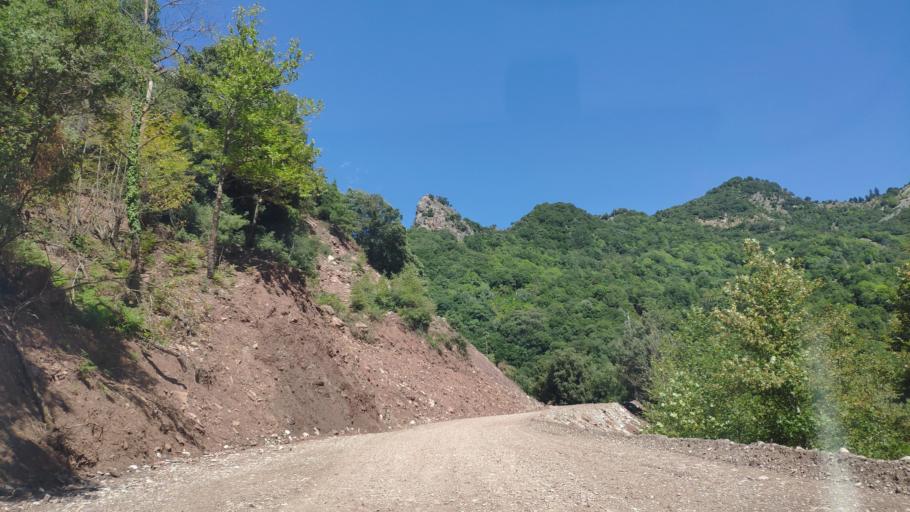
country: GR
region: Central Greece
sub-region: Nomos Evrytanias
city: Kerasochori
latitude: 39.0693
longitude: 21.6062
